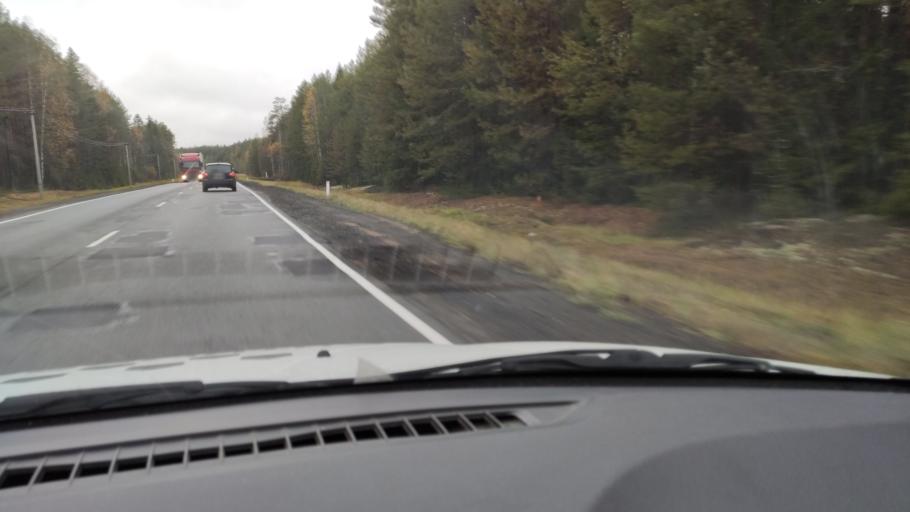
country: RU
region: Kirov
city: Belaya Kholunitsa
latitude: 58.9083
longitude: 50.9941
